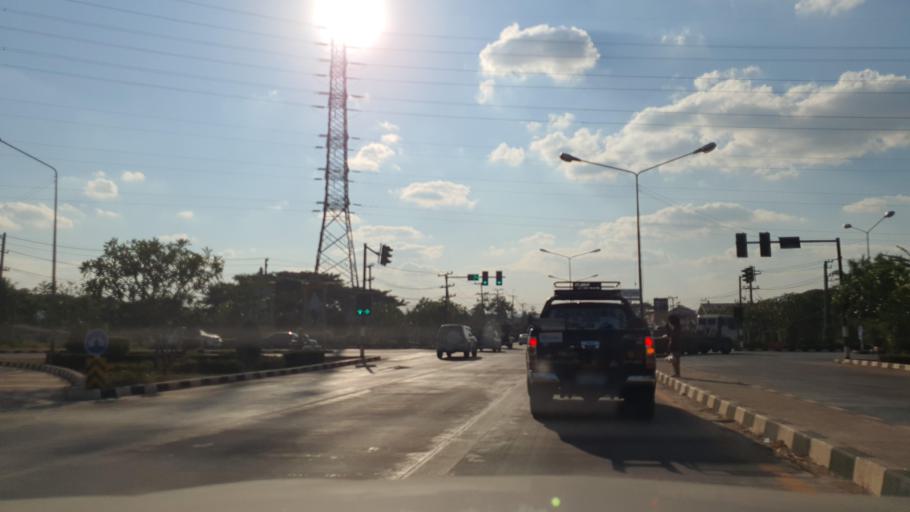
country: TH
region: Sakon Nakhon
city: Sakon Nakhon
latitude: 17.1421
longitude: 104.1113
